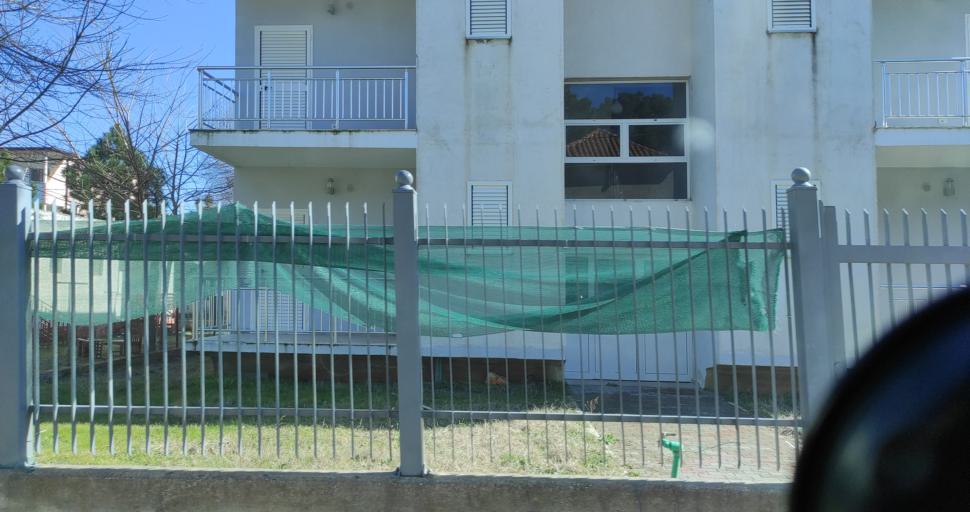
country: AL
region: Shkoder
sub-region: Rrethi i Shkodres
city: Velipoje
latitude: 41.8636
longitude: 19.4152
